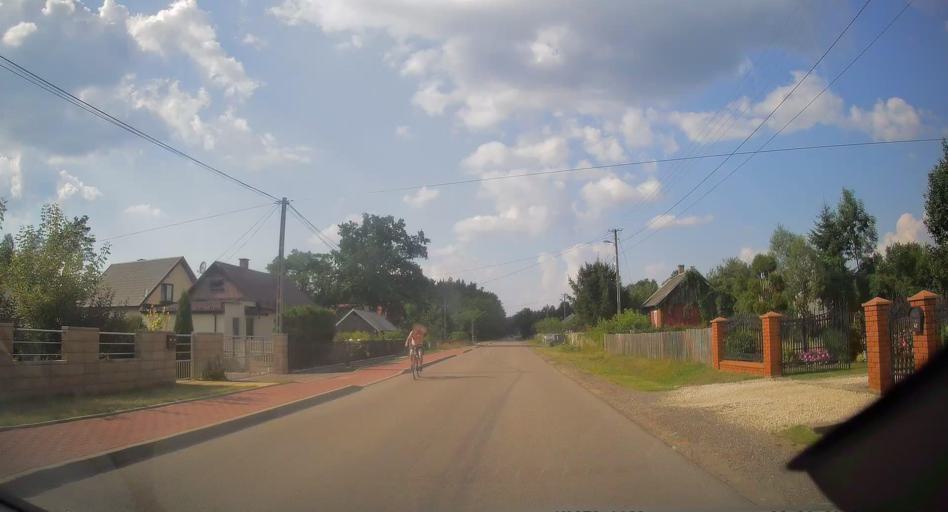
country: PL
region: Swietokrzyskie
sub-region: Powiat konecki
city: Ruda Maleniecka
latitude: 51.1195
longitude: 20.2596
